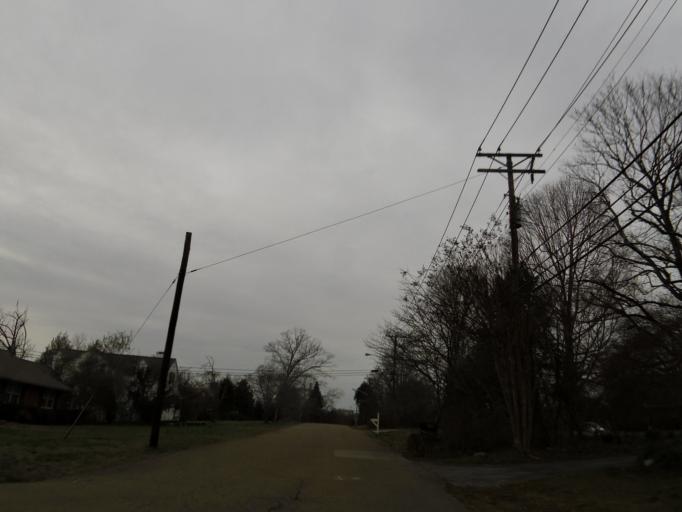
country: US
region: Tennessee
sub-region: Knox County
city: Knoxville
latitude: 36.0359
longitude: -83.9188
